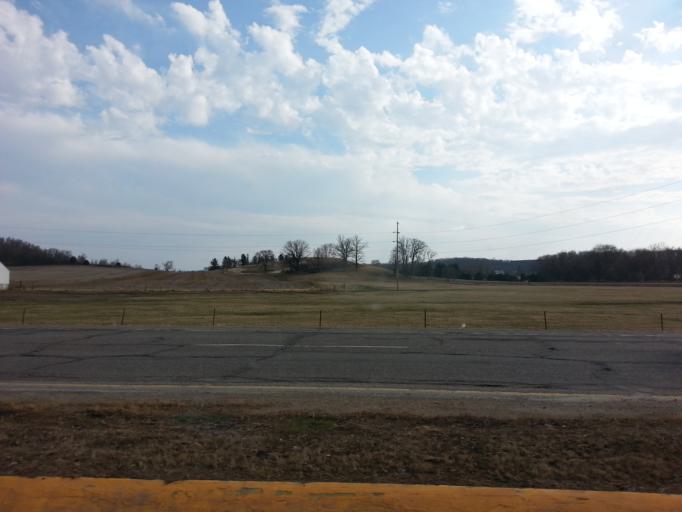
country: US
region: Wisconsin
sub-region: Pierce County
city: Ellsworth
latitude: 44.7329
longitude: -92.4547
